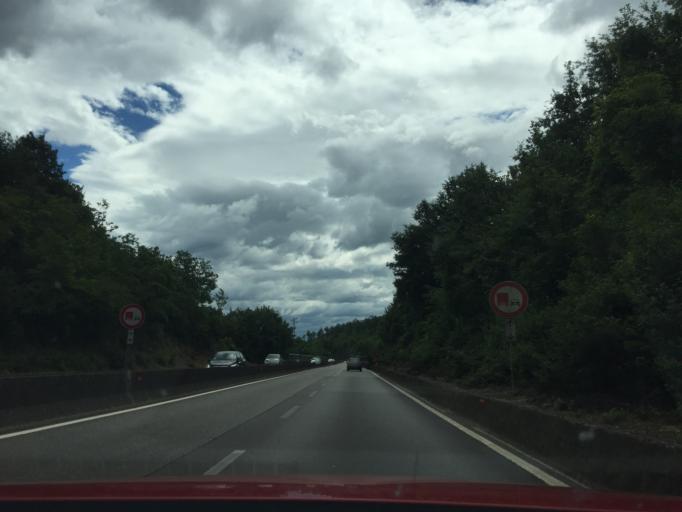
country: IT
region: Tuscany
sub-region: Province of Florence
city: Montelupo Fiorentino
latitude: 43.7187
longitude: 11.0311
